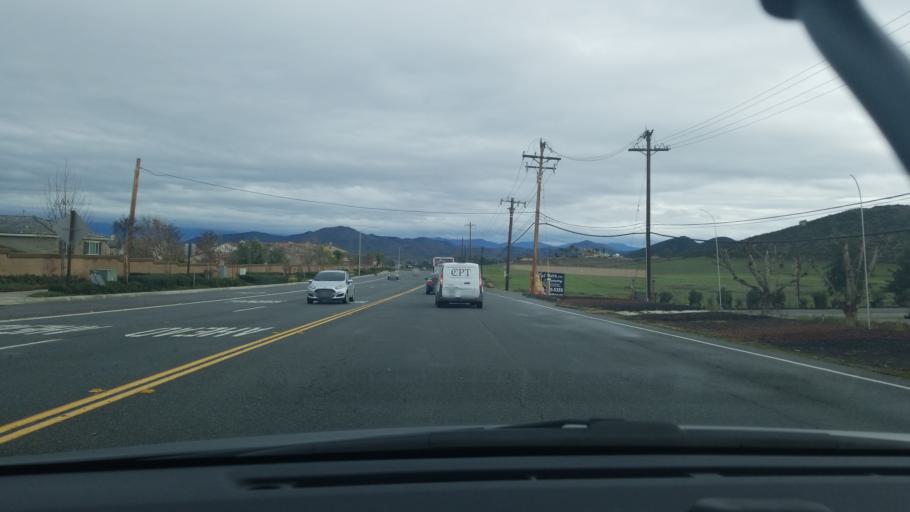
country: US
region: California
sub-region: Riverside County
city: Winchester
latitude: 33.6415
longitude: -117.1354
